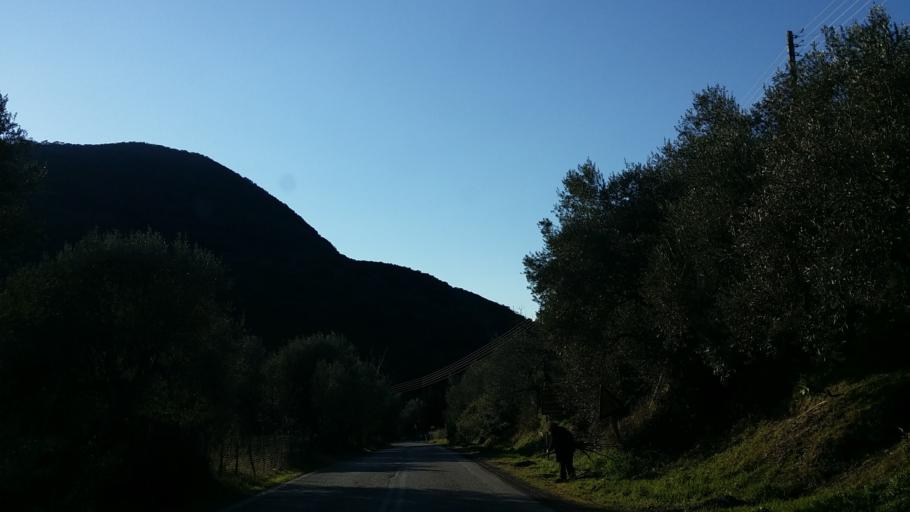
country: GR
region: West Greece
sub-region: Nomos Aitolias kai Akarnanias
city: Neapolis
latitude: 38.7942
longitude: 21.4491
